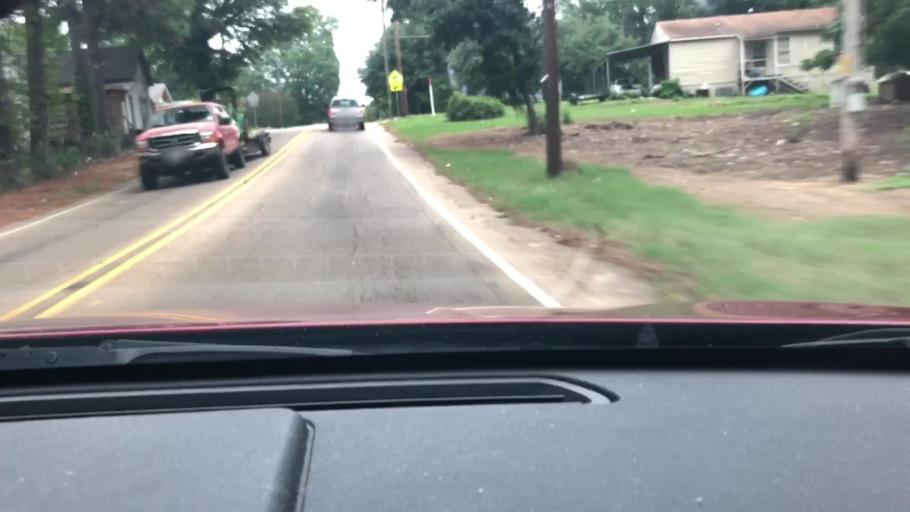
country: US
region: Arkansas
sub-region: Lafayette County
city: Stamps
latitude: 33.3655
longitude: -93.4940
